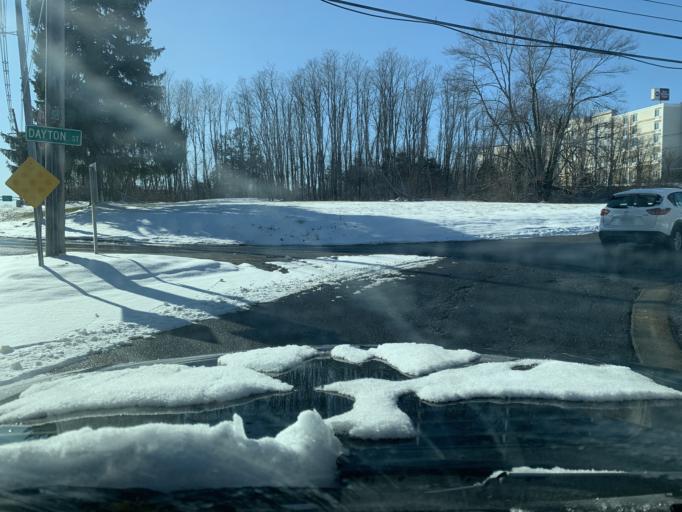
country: US
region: Massachusetts
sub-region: Essex County
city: Danvers
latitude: 42.5705
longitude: -70.9733
